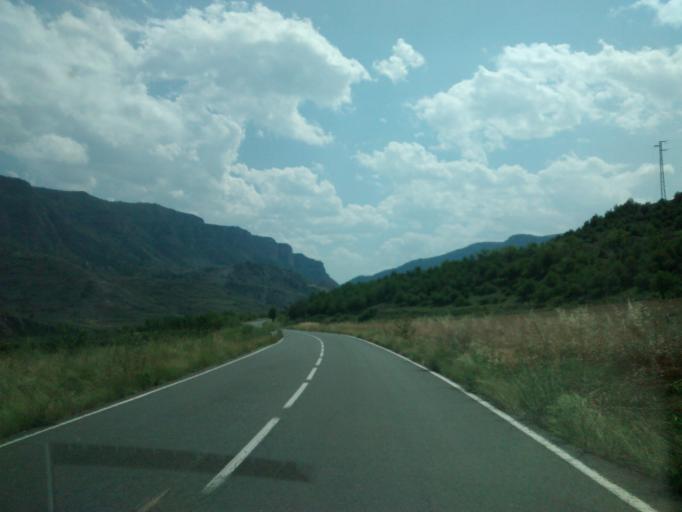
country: ES
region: La Rioja
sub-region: Provincia de La Rioja
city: Leza de Rio Leza
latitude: 42.3473
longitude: -2.3942
